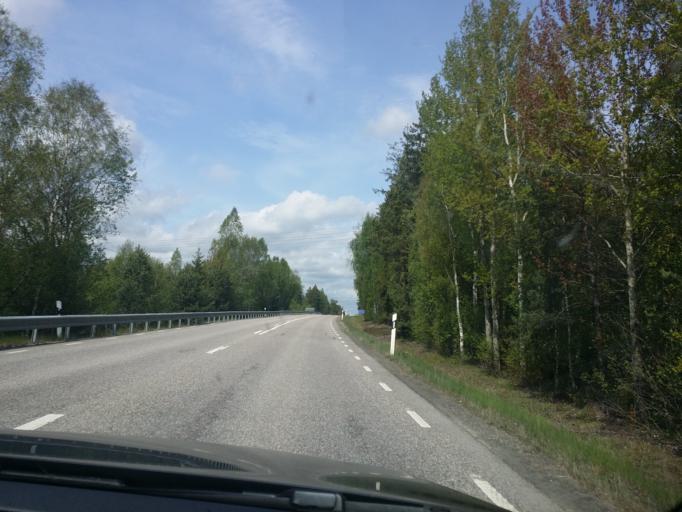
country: SE
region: Uppsala
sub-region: Habo Kommun
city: Balsta
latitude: 59.6375
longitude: 17.5774
